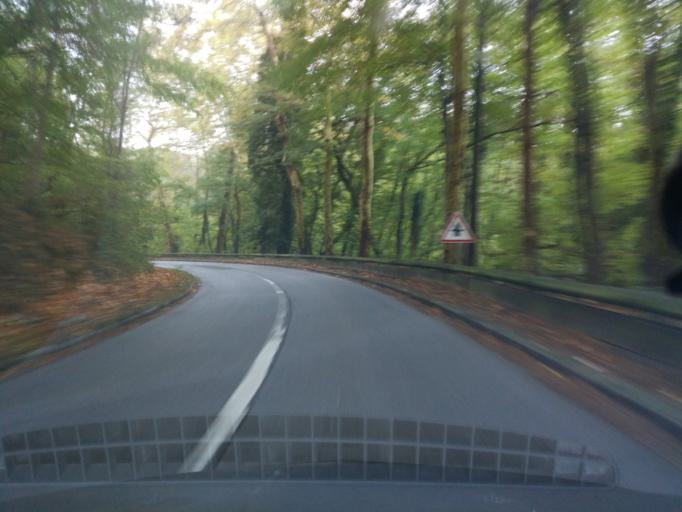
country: FR
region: Ile-de-France
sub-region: Departement de l'Essonne
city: Les Molieres
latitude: 48.6898
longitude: 2.0644
